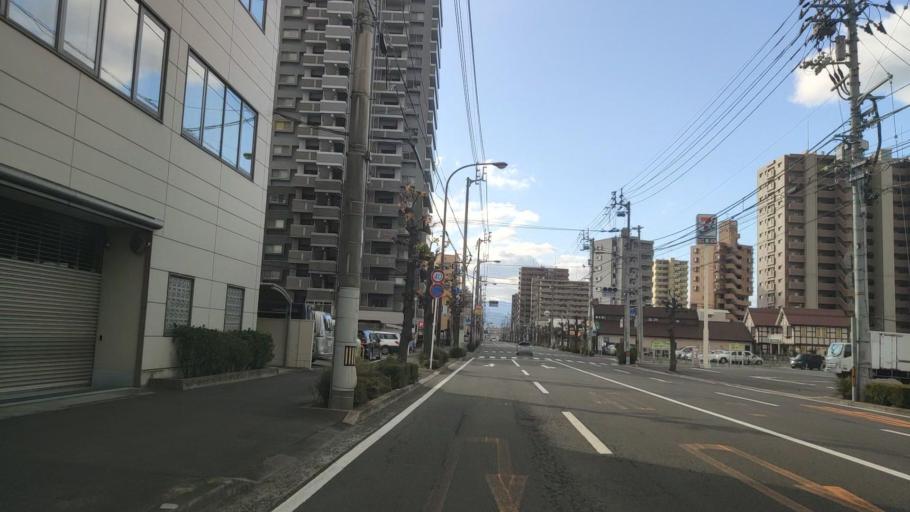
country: JP
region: Ehime
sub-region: Shikoku-chuo Shi
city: Matsuyama
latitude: 33.8352
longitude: 132.7525
